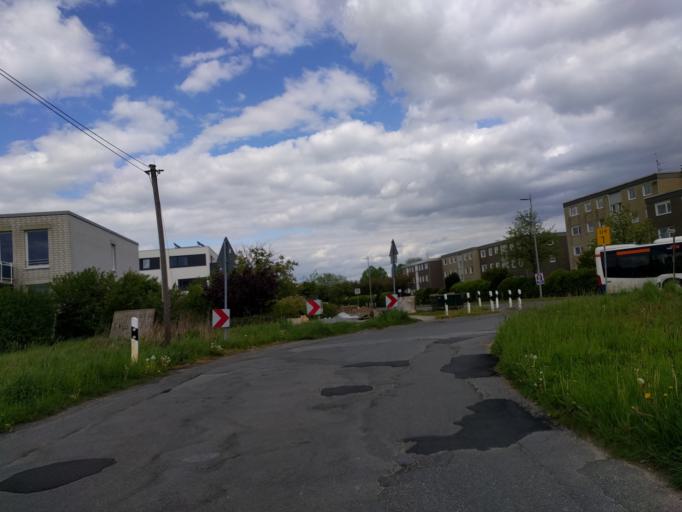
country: DE
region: North Rhine-Westphalia
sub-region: Regierungsbezirk Detmold
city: Bielefeld
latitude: 52.0487
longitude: 8.5004
